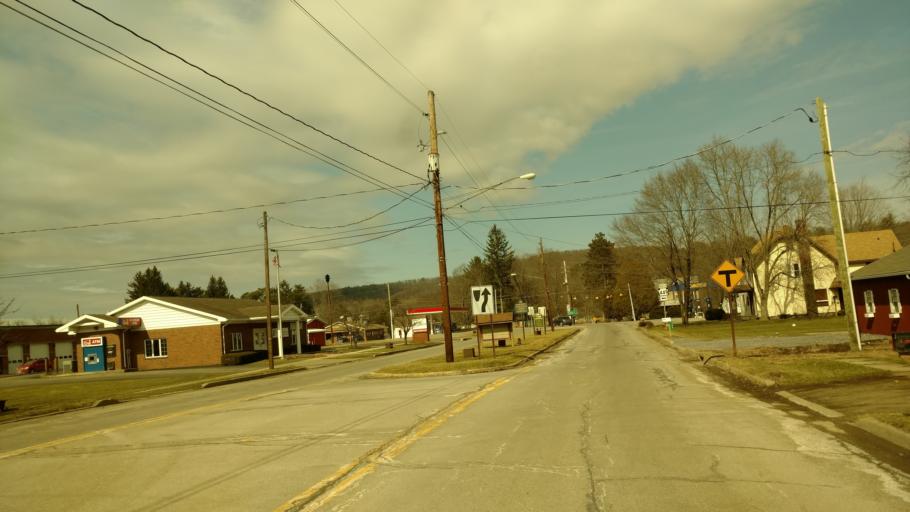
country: US
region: New York
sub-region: Allegany County
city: Wellsville
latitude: 41.9931
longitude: -77.8711
